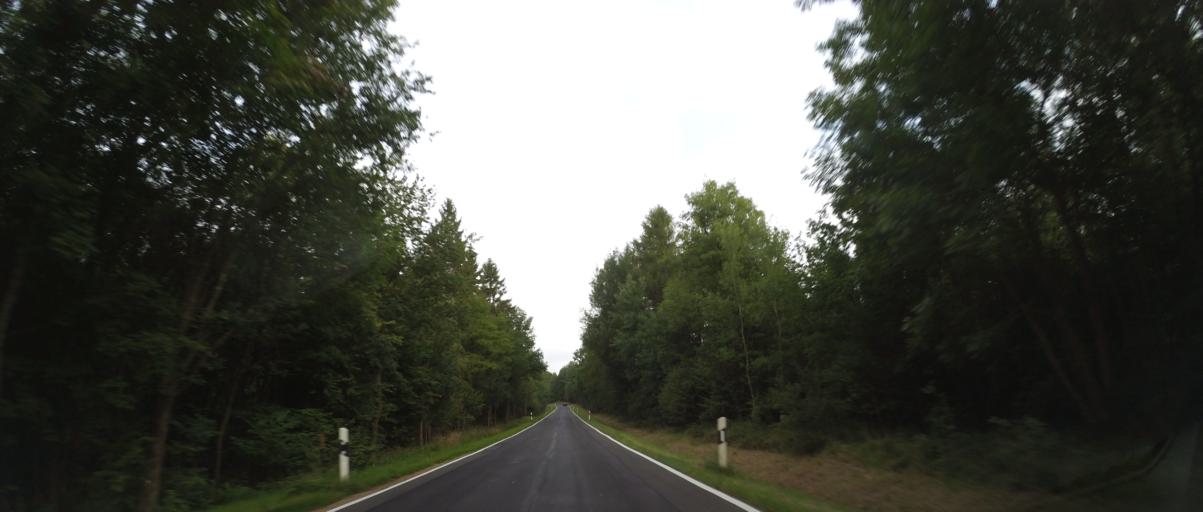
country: DE
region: Rheinland-Pfalz
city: Bongard
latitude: 50.3013
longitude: 6.8176
